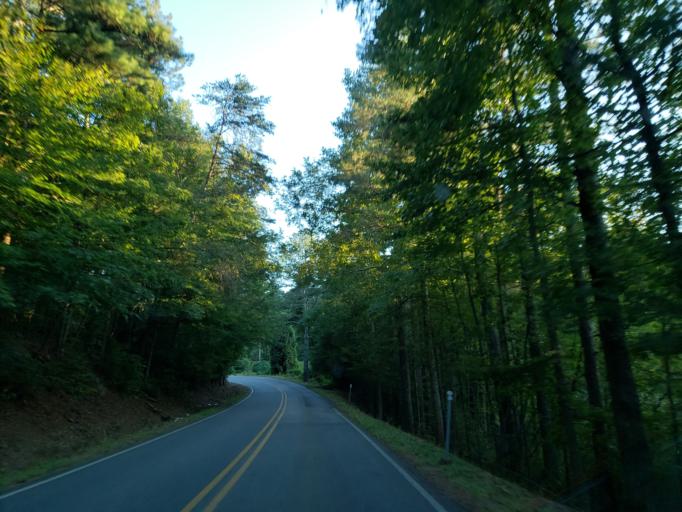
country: US
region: Georgia
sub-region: Bartow County
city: Rydal
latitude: 34.3485
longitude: -84.5837
